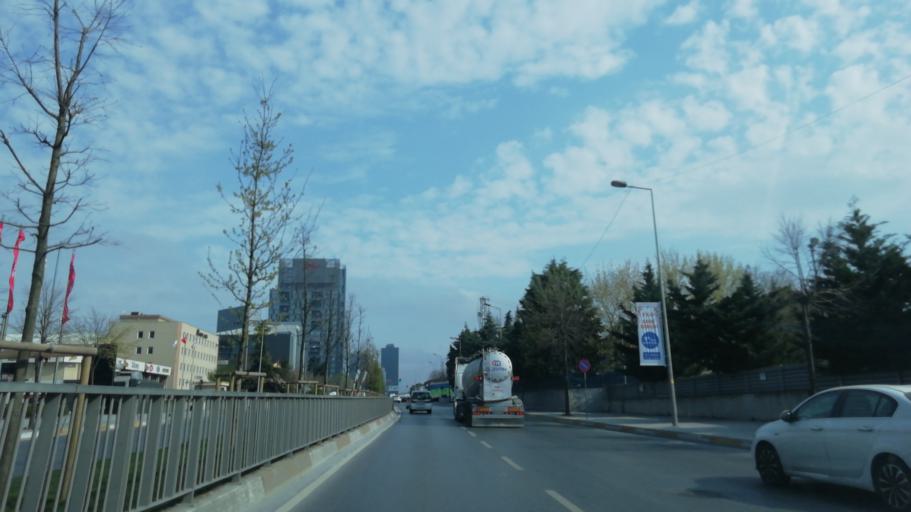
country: TR
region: Istanbul
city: Mahmutbey
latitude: 41.0475
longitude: 28.8122
